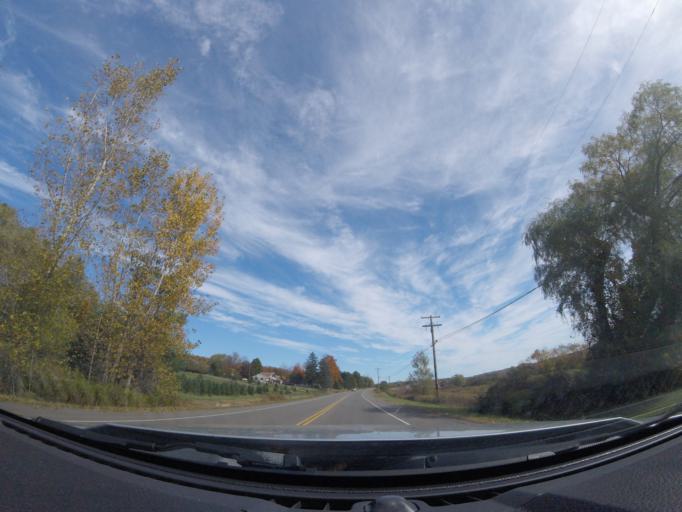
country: US
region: New York
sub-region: Tompkins County
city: Dryden
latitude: 42.5563
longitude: -76.2819
